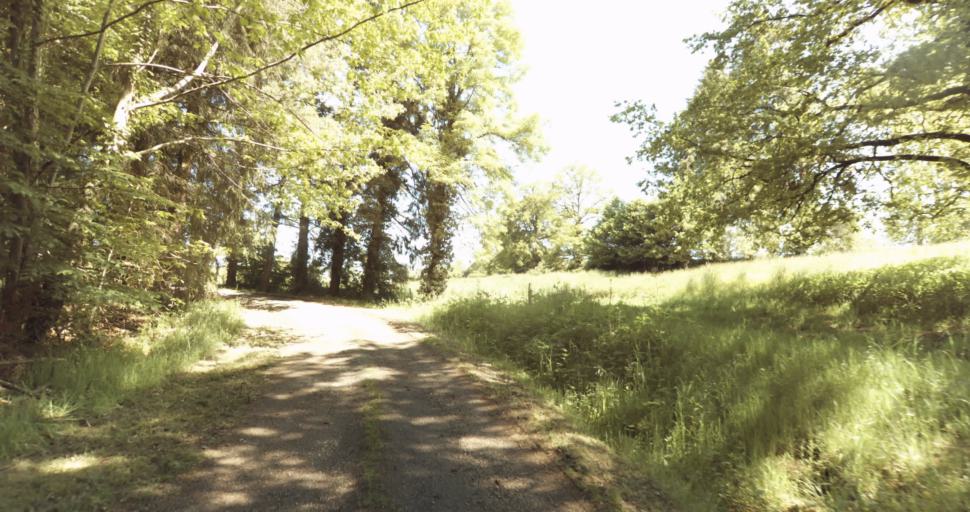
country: FR
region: Limousin
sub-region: Departement de la Haute-Vienne
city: Le Vigen
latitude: 45.7309
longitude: 1.2908
